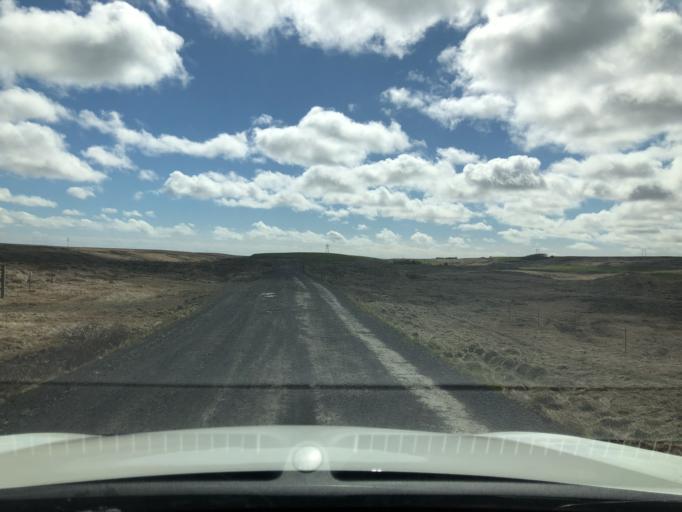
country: IS
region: South
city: Selfoss
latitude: 63.9306
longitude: -20.6700
